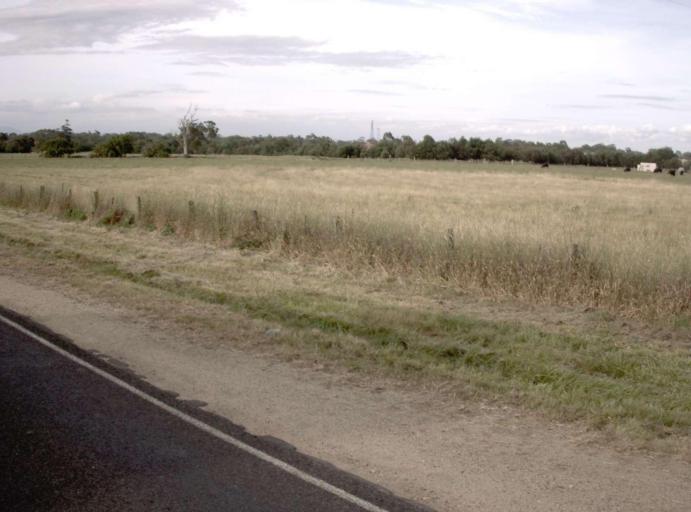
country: AU
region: Victoria
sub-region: Wellington
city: Heyfield
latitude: -37.9950
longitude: 146.7771
